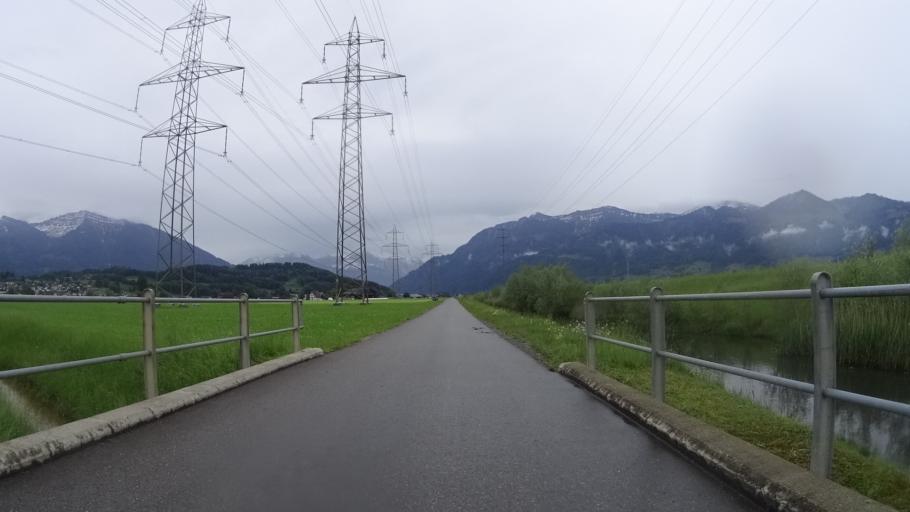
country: CH
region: Saint Gallen
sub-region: Wahlkreis See-Gaster
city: Uznach
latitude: 47.2048
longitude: 8.9810
